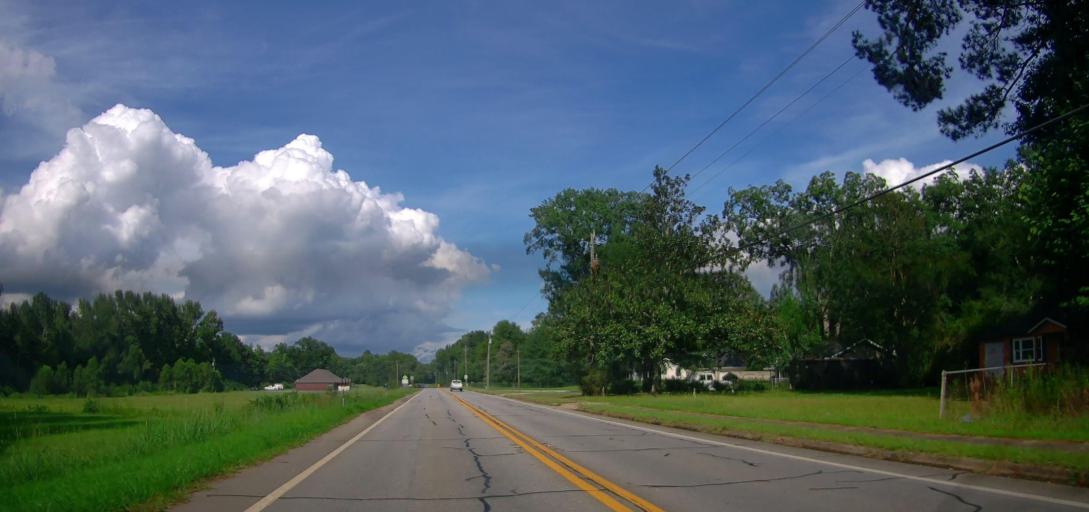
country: US
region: Georgia
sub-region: Harris County
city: Hamilton
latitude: 32.6426
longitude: -84.8826
